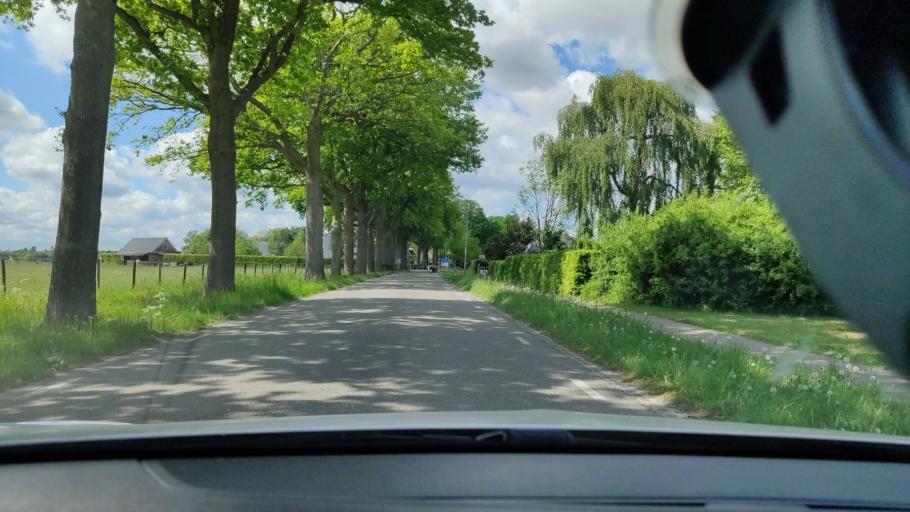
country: NL
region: Drenthe
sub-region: Gemeente Tynaarlo
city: Zuidlaren
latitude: 53.1165
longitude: 6.6703
